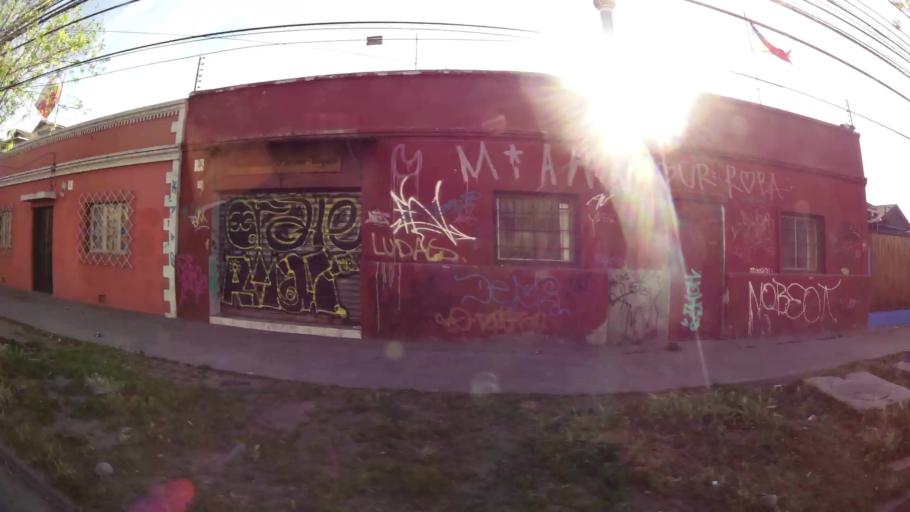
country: CL
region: Santiago Metropolitan
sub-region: Provincia de Cordillera
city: Puente Alto
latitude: -33.6105
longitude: -70.5704
